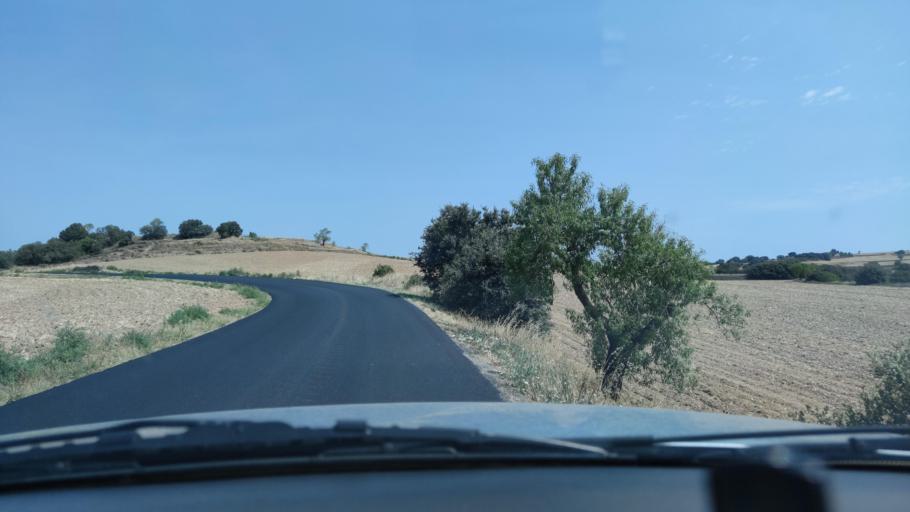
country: ES
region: Catalonia
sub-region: Provincia de Lleida
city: Ivorra
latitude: 41.7706
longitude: 1.3269
